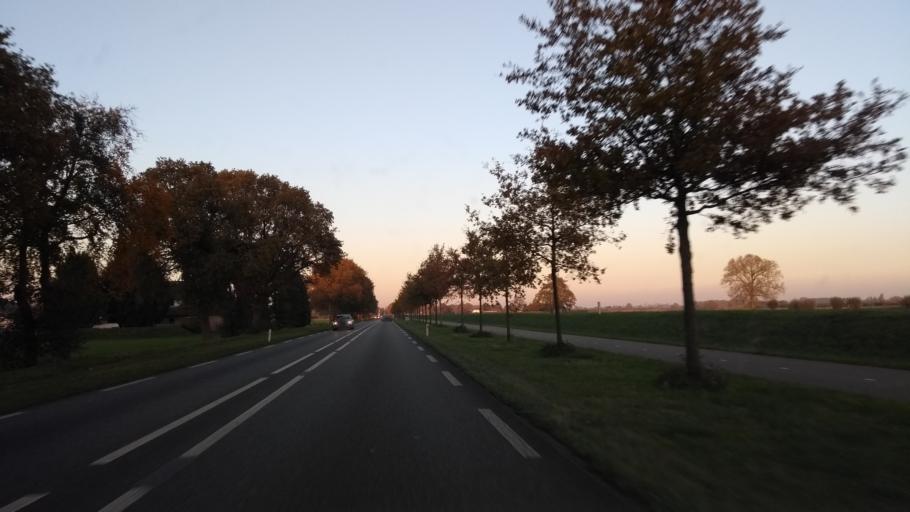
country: NL
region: Gelderland
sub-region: Gemeente Rheden
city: Spankeren
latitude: 52.0669
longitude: 6.1327
